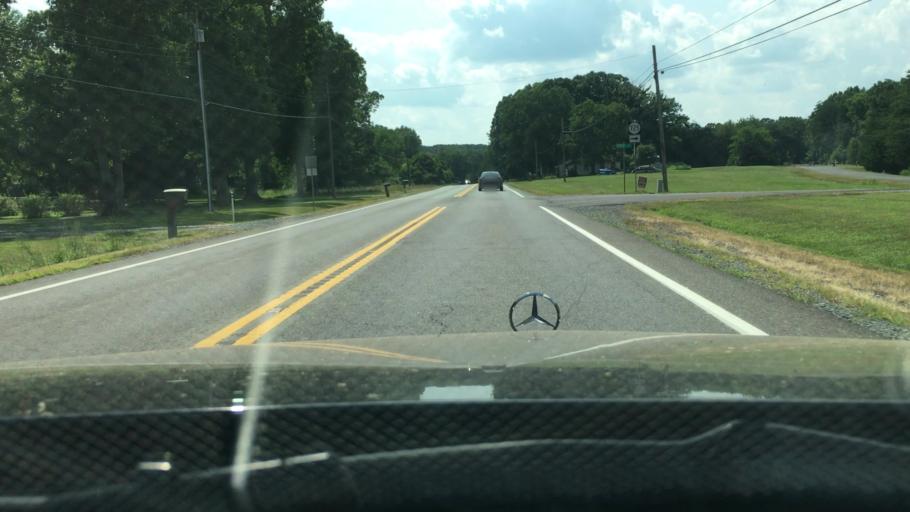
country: US
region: Virginia
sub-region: Orange County
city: Orange
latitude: 38.2583
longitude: -78.0016
